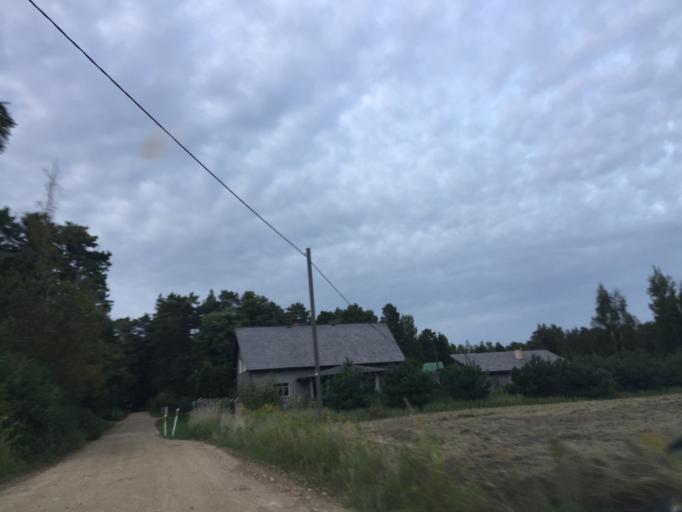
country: LV
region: Saulkrastu
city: Saulkrasti
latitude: 57.3293
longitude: 24.4075
